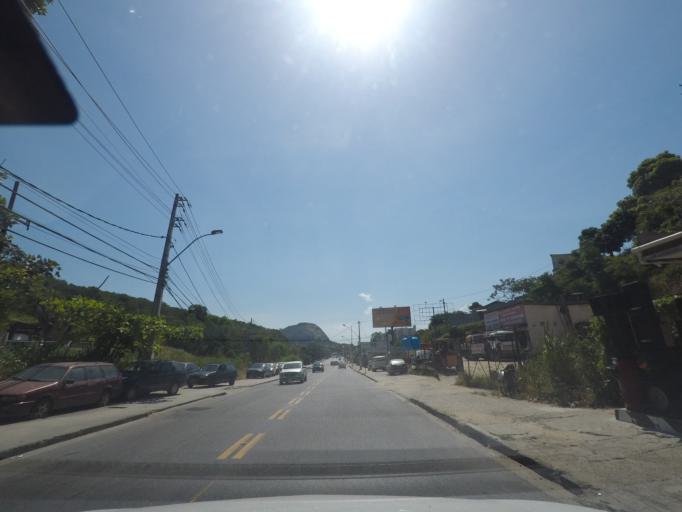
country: BR
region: Rio de Janeiro
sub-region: Niteroi
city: Niteroi
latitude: -22.9108
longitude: -43.0545
